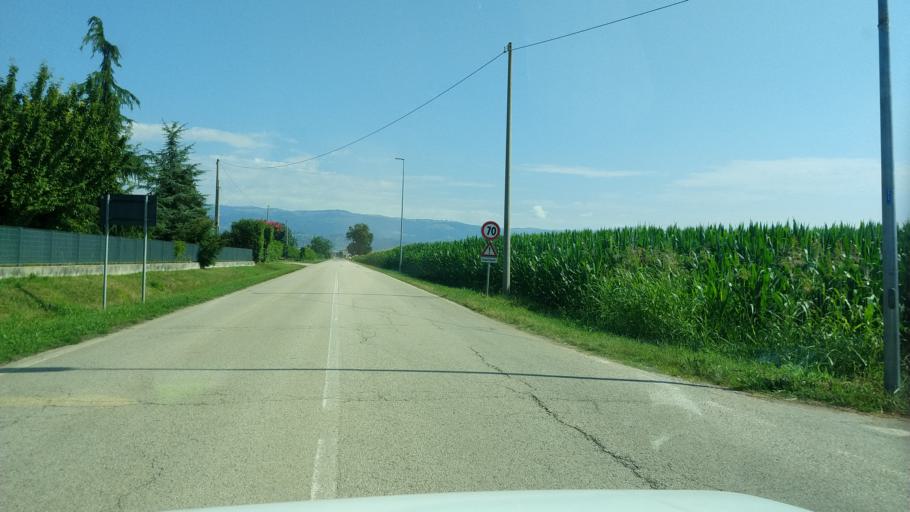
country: IT
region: Veneto
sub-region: Provincia di Vicenza
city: Sandrigo
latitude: 45.6666
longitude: 11.6069
